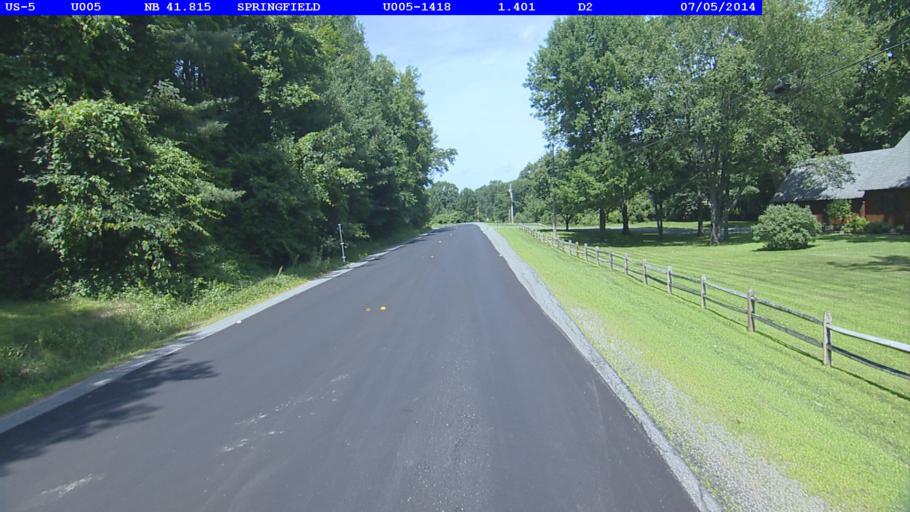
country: US
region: New Hampshire
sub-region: Sullivan County
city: Charlestown
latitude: 43.2532
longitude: -72.4397
